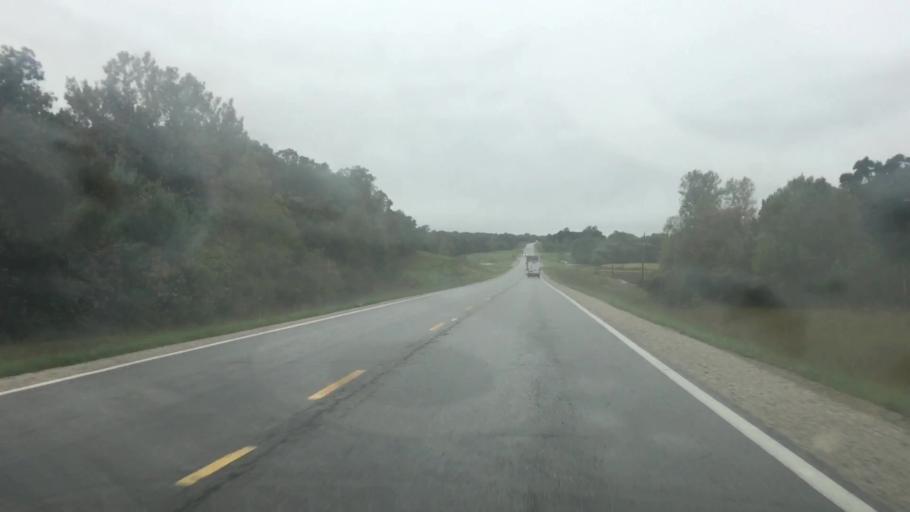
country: US
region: Kansas
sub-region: Anderson County
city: Garnett
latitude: 38.2157
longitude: -95.2488
